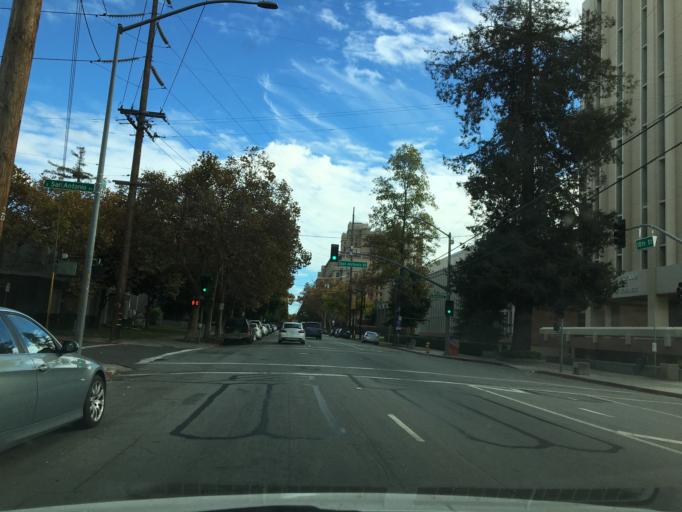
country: US
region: California
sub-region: Santa Clara County
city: San Jose
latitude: 37.3377
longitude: -121.8788
